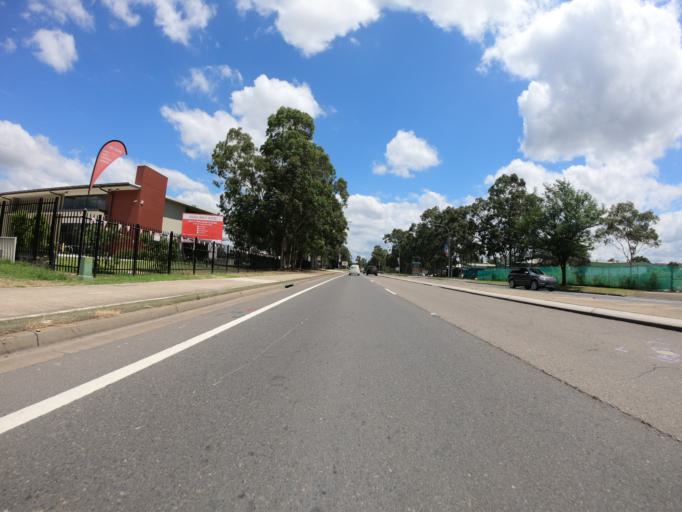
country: AU
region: New South Wales
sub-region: Penrith Municipality
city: Glenmore Park
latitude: -33.7667
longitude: 150.6792
